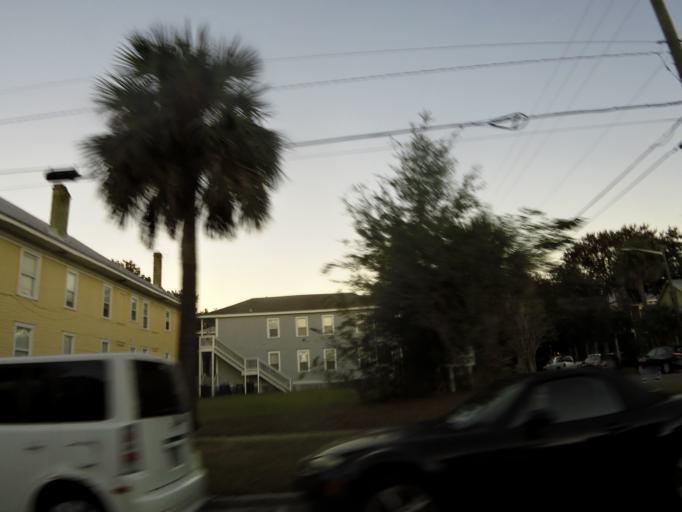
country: US
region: Florida
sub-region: Duval County
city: Jacksonville
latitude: 30.3403
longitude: -81.6514
